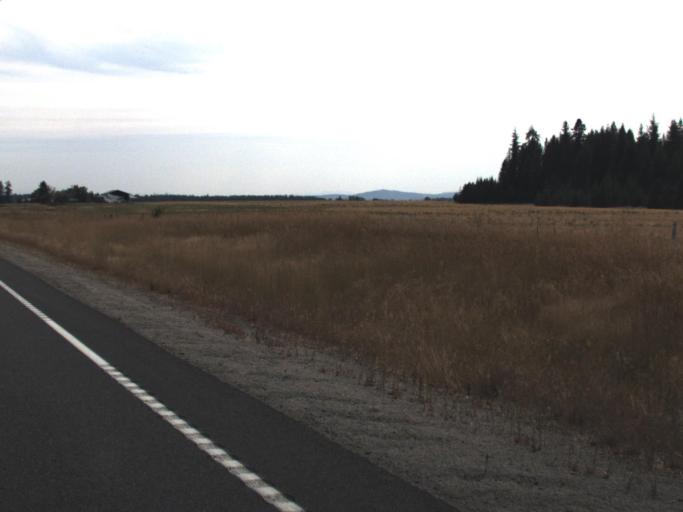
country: US
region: Washington
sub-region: Spokane County
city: Deer Park
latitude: 47.9828
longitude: -117.5299
